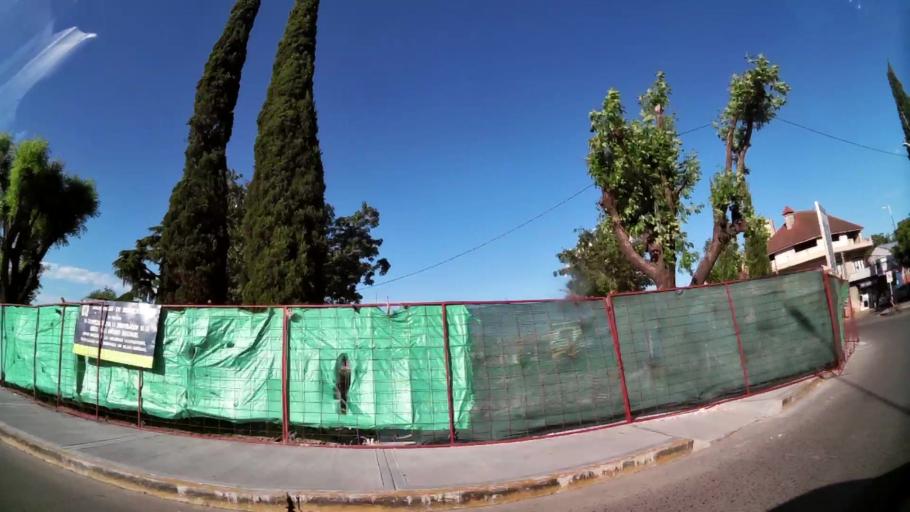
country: AR
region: Buenos Aires
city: Santa Catalina - Dique Lujan
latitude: -34.4891
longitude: -58.7267
